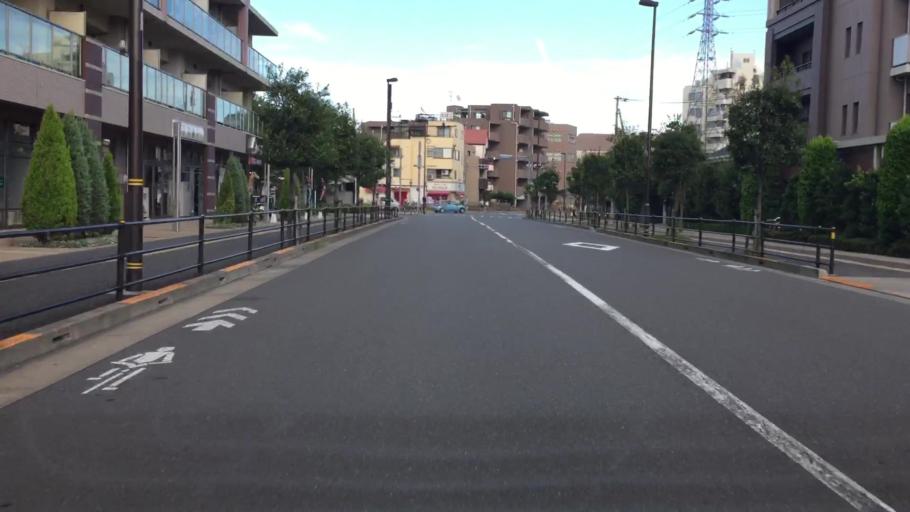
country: JP
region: Saitama
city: Soka
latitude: 35.7709
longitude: 139.7952
